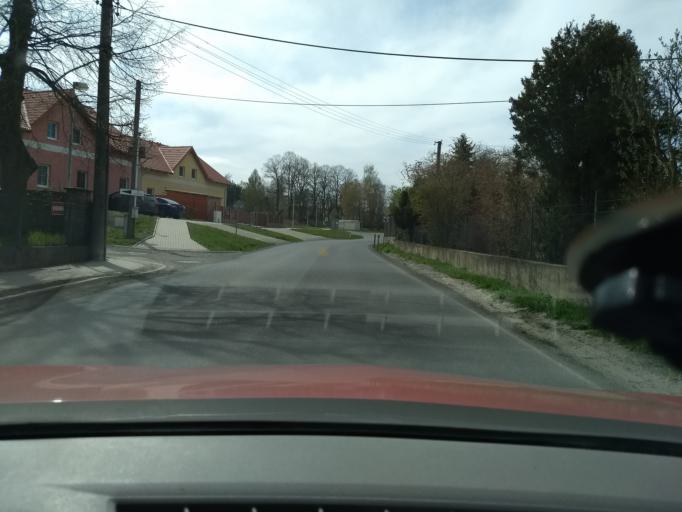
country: CZ
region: Central Bohemia
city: Rudna
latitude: 50.0599
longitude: 14.2267
